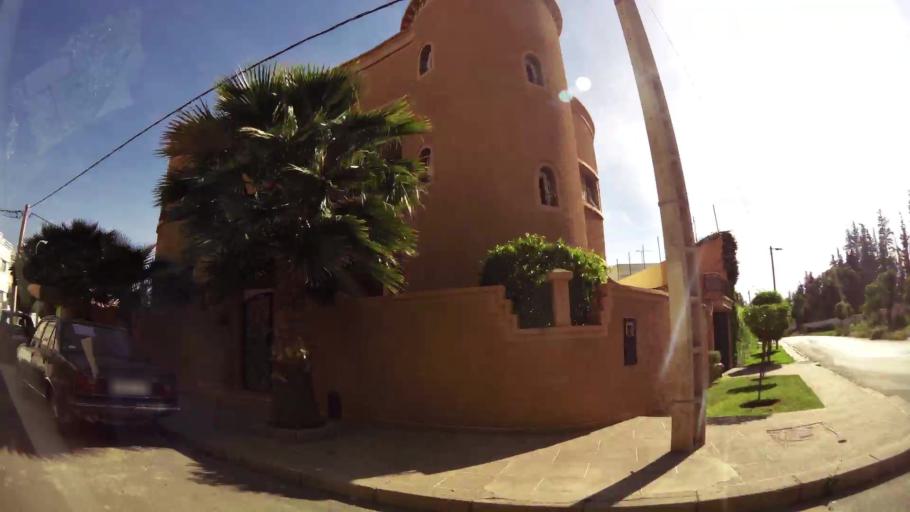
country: MA
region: Oriental
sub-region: Oujda-Angad
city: Oujda
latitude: 34.6661
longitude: -1.9004
